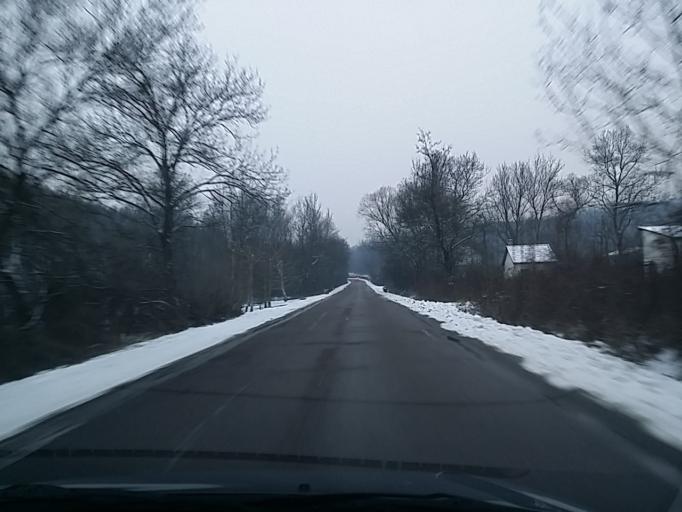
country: HU
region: Heves
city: Sirok
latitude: 47.9098
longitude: 20.1781
